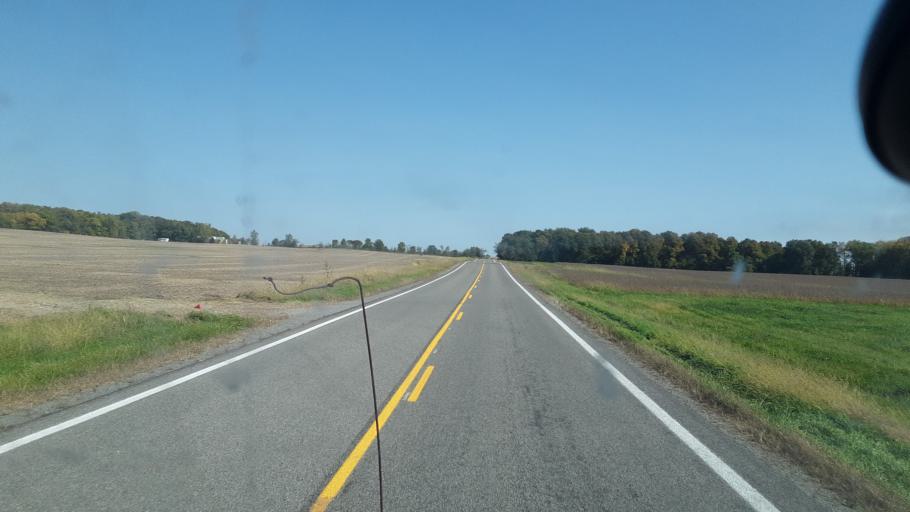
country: US
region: Ohio
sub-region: Logan County
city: Northwood
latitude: 40.5080
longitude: -83.6536
